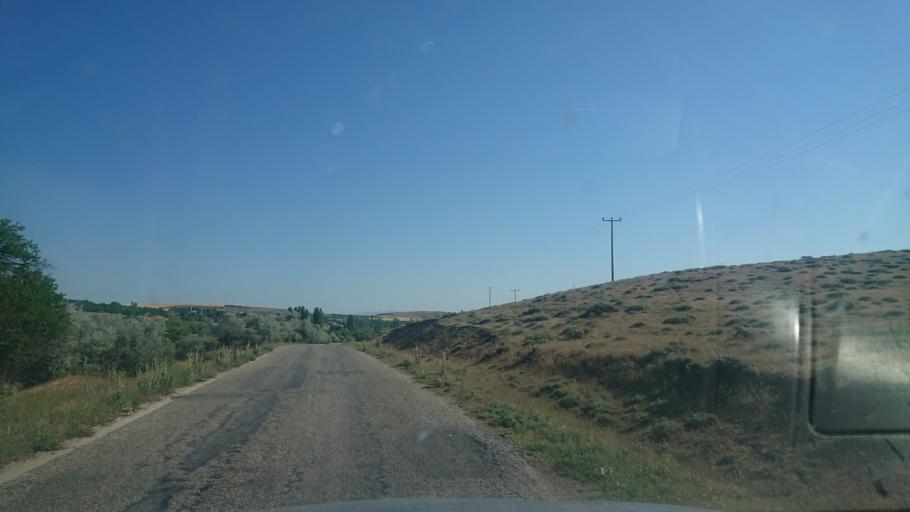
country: TR
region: Aksaray
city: Agacoren
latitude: 38.8760
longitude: 33.8807
